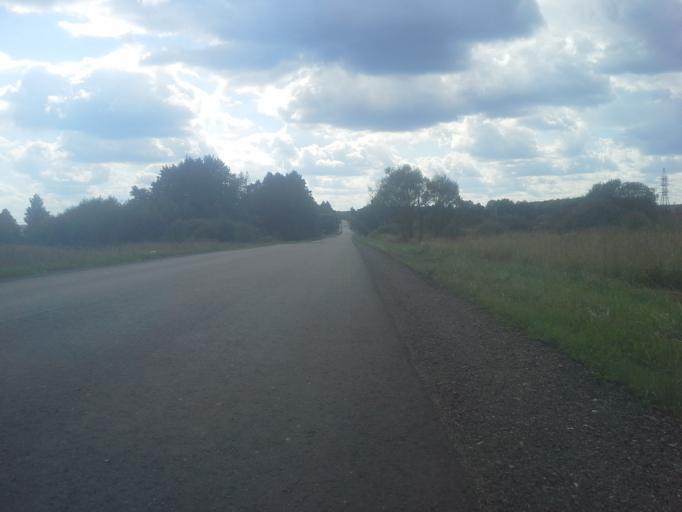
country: RU
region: Moskovskaya
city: Selyatino
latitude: 55.3248
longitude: 37.0838
